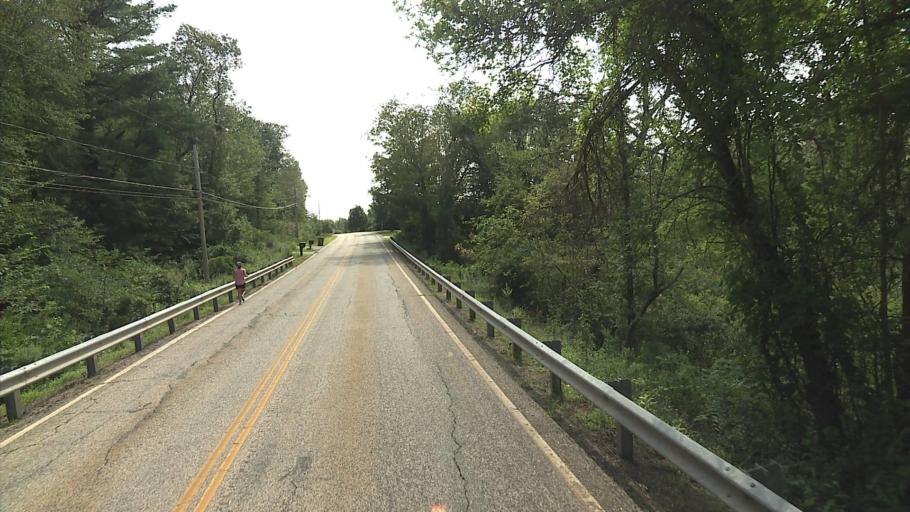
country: US
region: Connecticut
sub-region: New London County
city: Colchester
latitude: 41.5740
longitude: -72.2705
